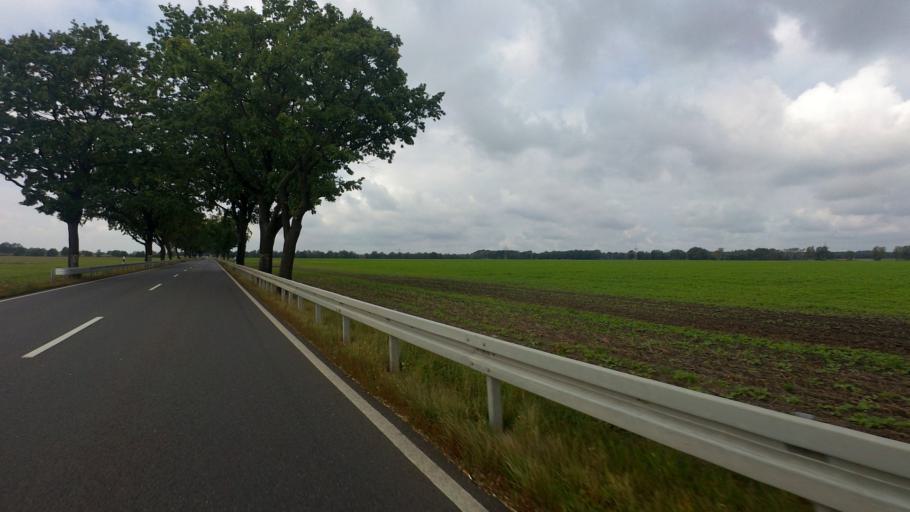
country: DE
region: Brandenburg
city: Tettau
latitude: 51.4670
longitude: 13.7212
